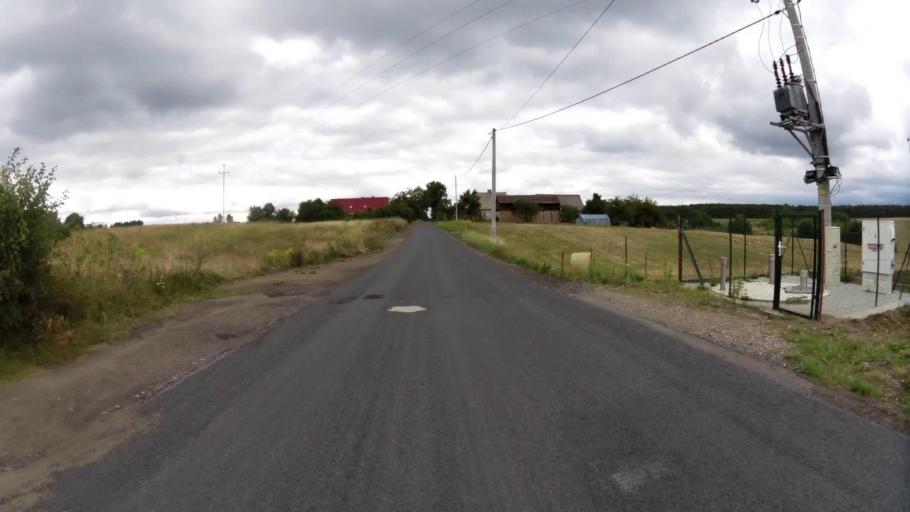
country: PL
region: West Pomeranian Voivodeship
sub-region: Powiat mysliborski
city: Debno
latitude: 52.7712
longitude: 14.6990
